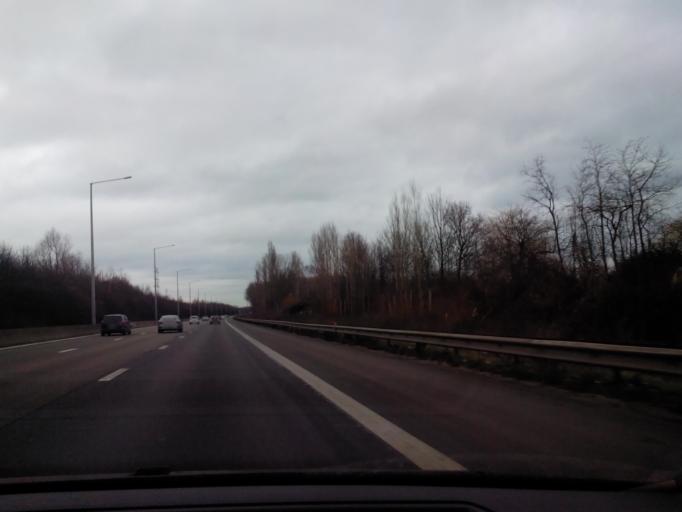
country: BE
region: Flanders
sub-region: Provincie Antwerpen
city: Rumst
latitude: 51.1055
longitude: 4.4341
